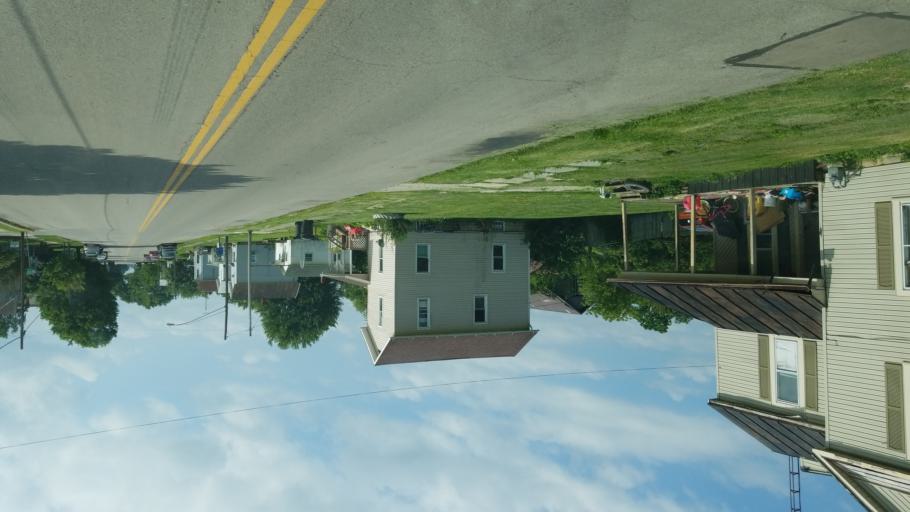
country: US
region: Ohio
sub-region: Richland County
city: Shelby
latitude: 40.9085
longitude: -82.7723
